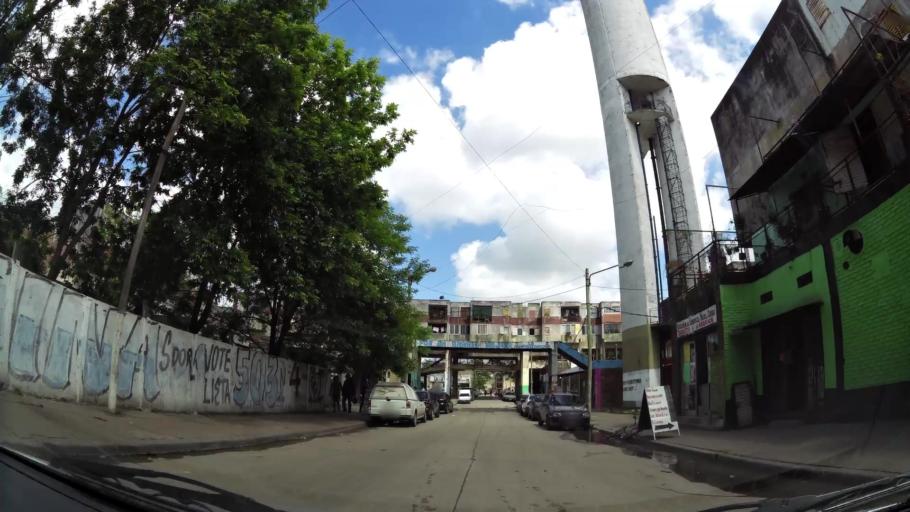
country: AR
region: Buenos Aires
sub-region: Partido de Quilmes
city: Quilmes
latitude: -34.8325
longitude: -58.2216
